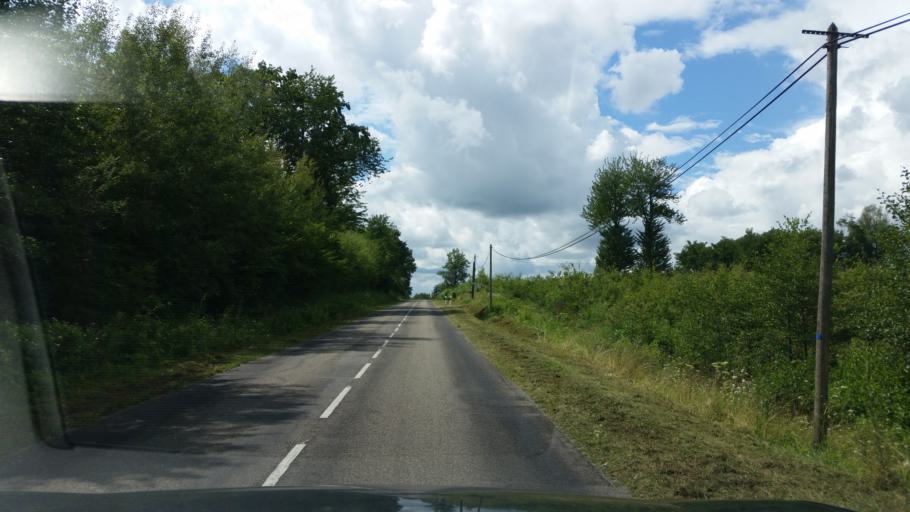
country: FR
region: Bourgogne
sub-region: Departement de Saone-et-Loire
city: Sagy
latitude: 46.6915
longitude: 5.3641
